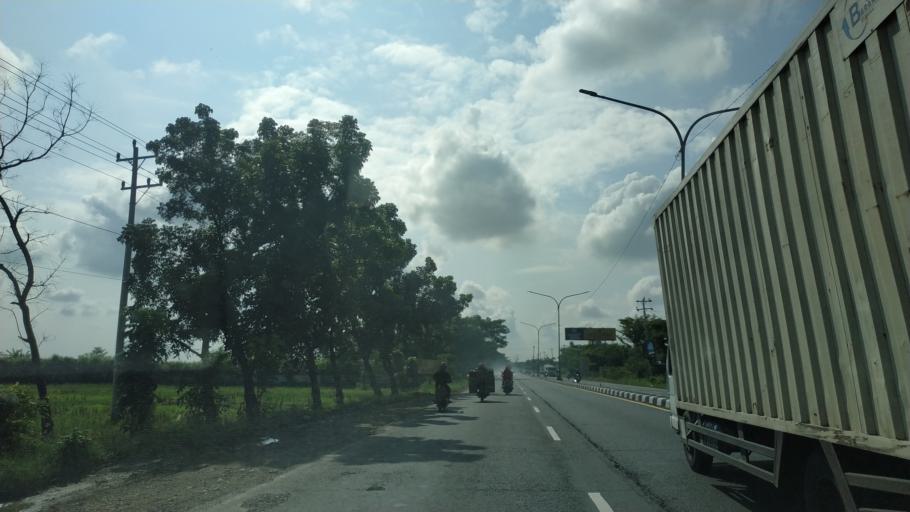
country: ID
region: Central Java
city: Comal
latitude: -6.9006
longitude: 109.5024
